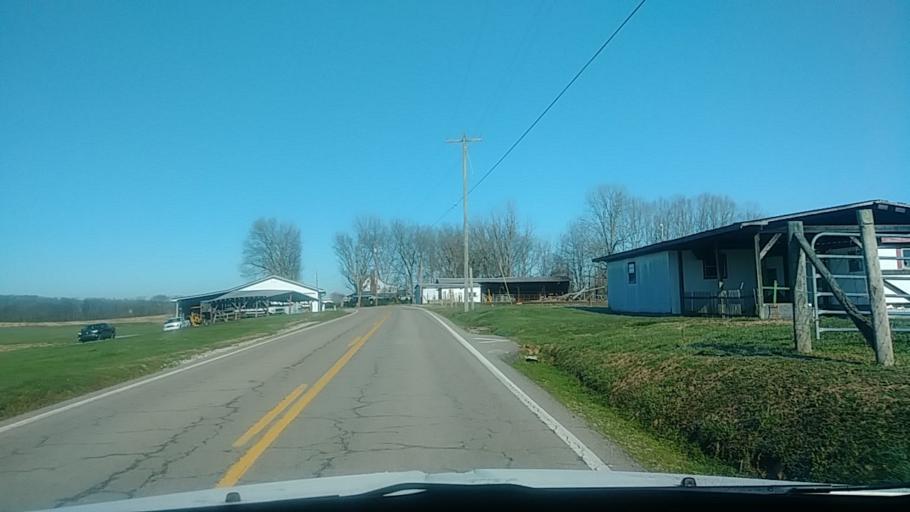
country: US
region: Tennessee
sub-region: Jefferson County
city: White Pine
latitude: 36.1477
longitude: -83.1486
